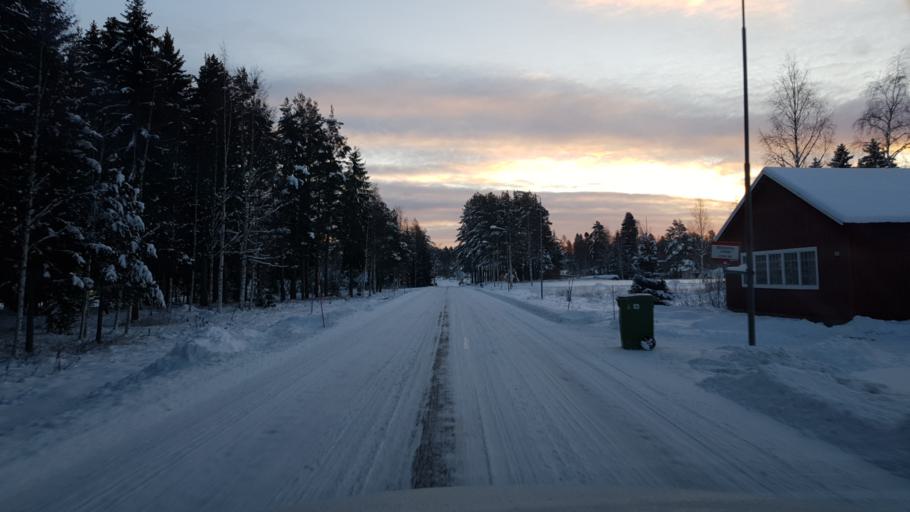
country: SE
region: Gaevleborg
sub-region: Ovanakers Kommun
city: Alfta
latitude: 61.3401
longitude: 15.9440
